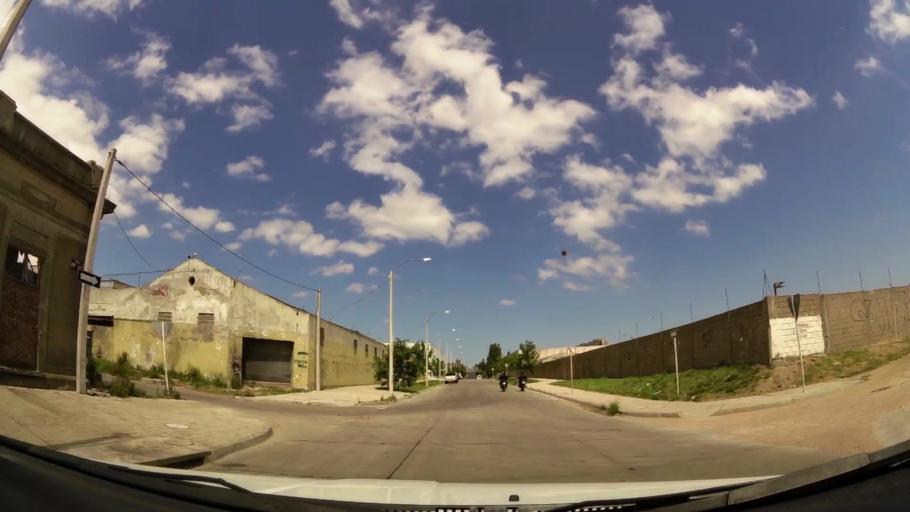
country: UY
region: Montevideo
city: Montevideo
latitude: -34.8466
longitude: -56.2367
